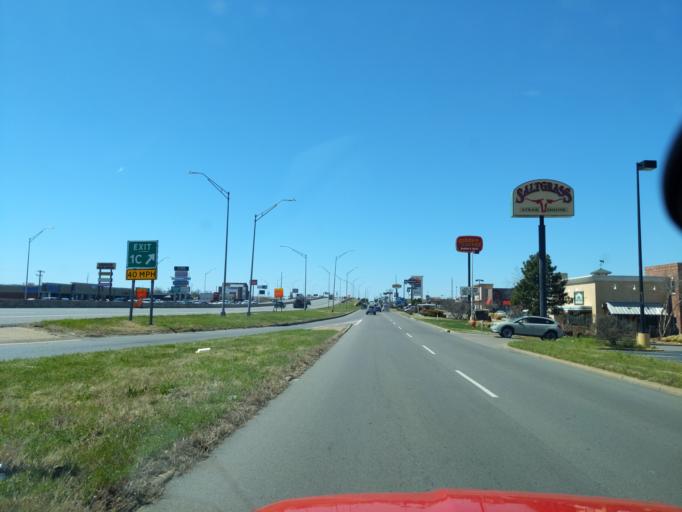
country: US
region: Oklahoma
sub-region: Cleveland County
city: Moore
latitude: 35.3918
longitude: -97.5427
